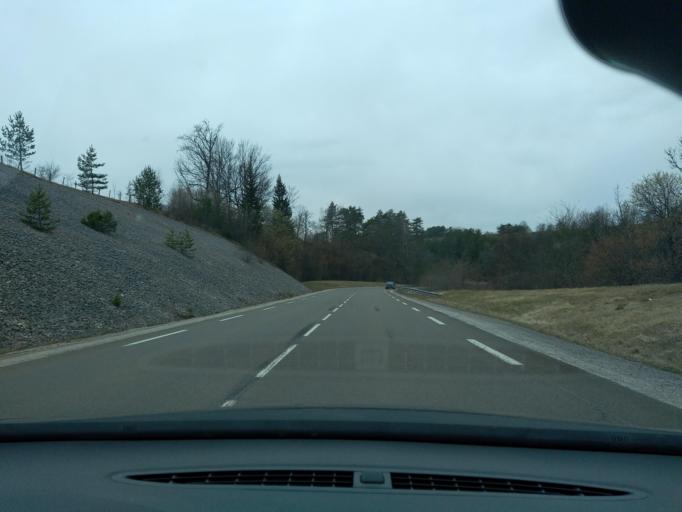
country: FR
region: Franche-Comte
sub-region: Departement du Jura
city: Arinthod
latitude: 46.4096
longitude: 5.5631
